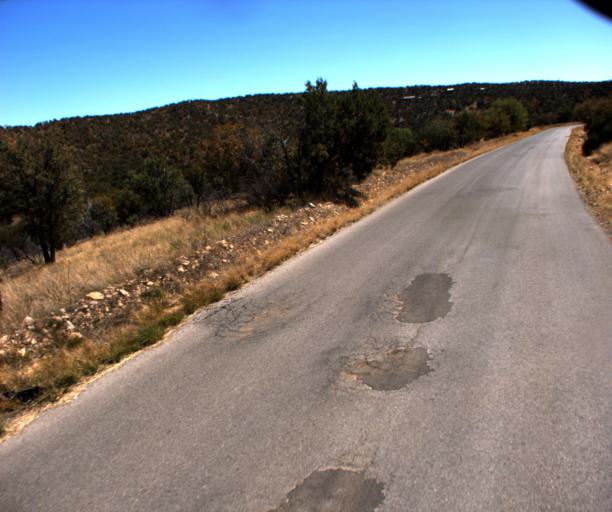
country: US
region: Arizona
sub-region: Cochise County
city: Sierra Vista
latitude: 31.4362
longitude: -110.4394
